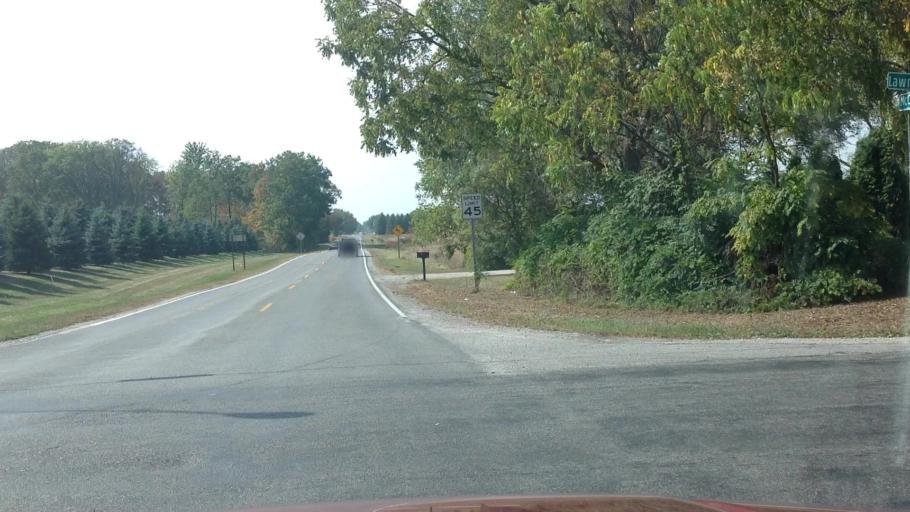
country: US
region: Michigan
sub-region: Saginaw County
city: Shields
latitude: 43.4661
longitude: -84.0340
